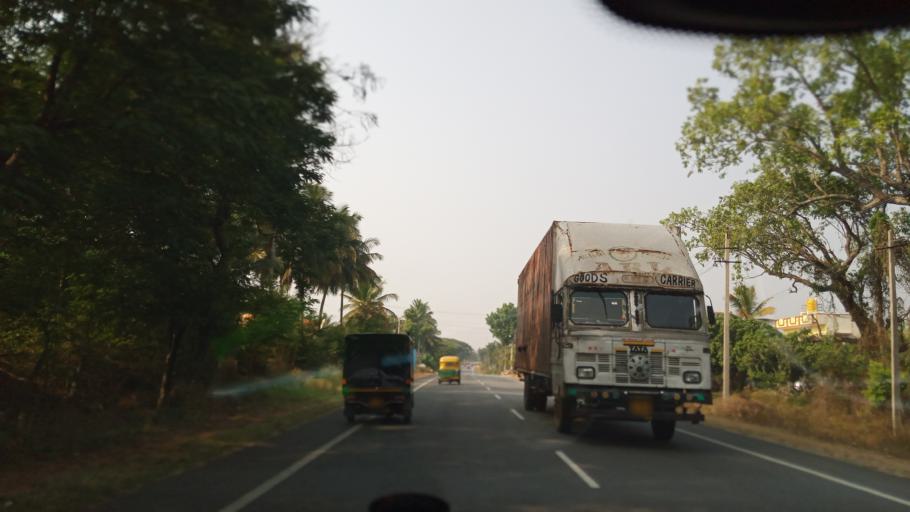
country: IN
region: Karnataka
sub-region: Mandya
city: Belluru
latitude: 12.9310
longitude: 76.7497
